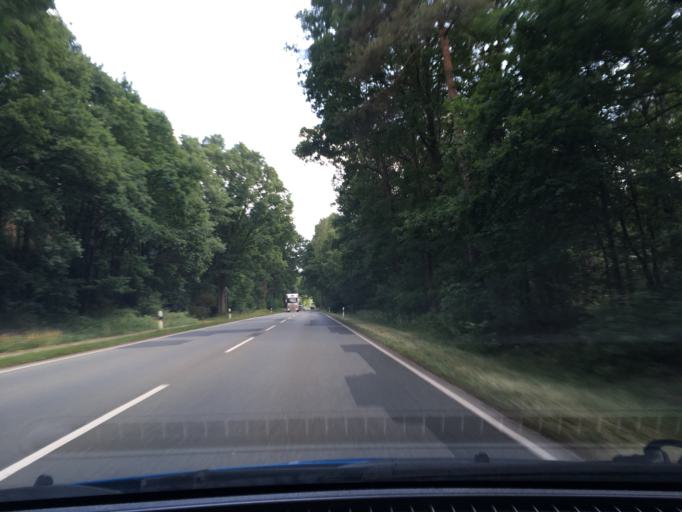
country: DE
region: Lower Saxony
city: Welle
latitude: 53.2611
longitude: 9.8044
